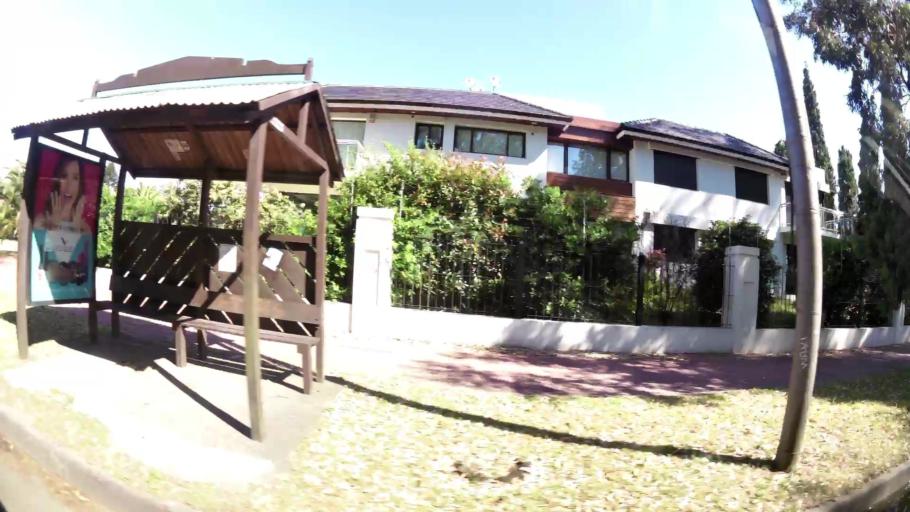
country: UY
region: Canelones
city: Paso de Carrasco
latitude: -34.8876
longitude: -56.0625
